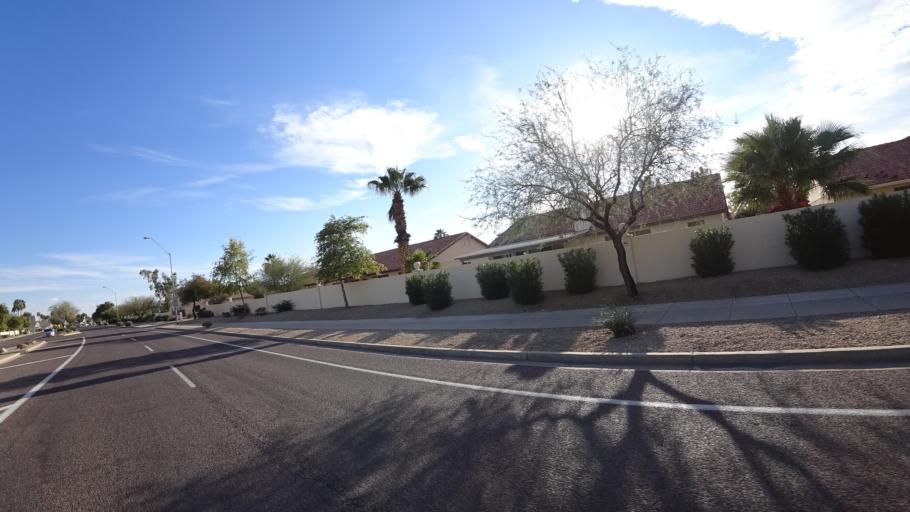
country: US
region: Arizona
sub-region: Maricopa County
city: Sun City
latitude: 33.6197
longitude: -112.2550
